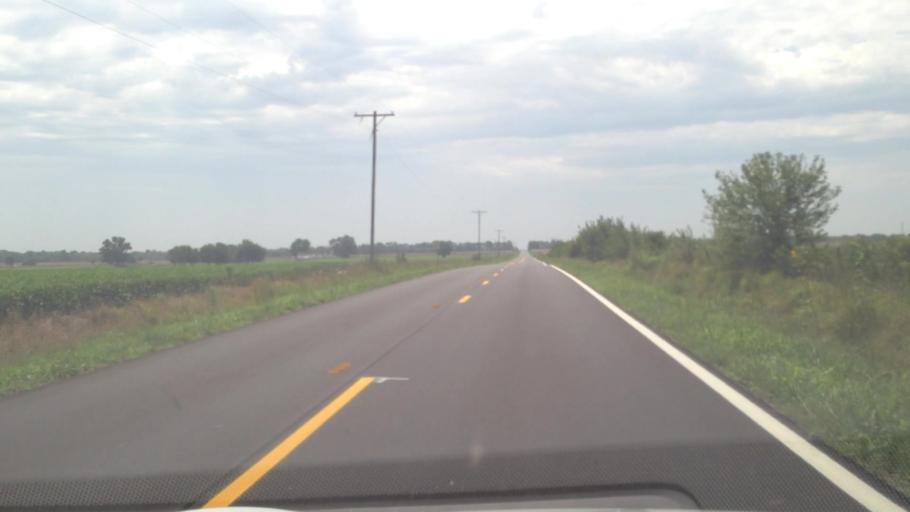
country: US
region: Kansas
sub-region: Crawford County
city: Girard
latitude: 37.6485
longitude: -94.9698
